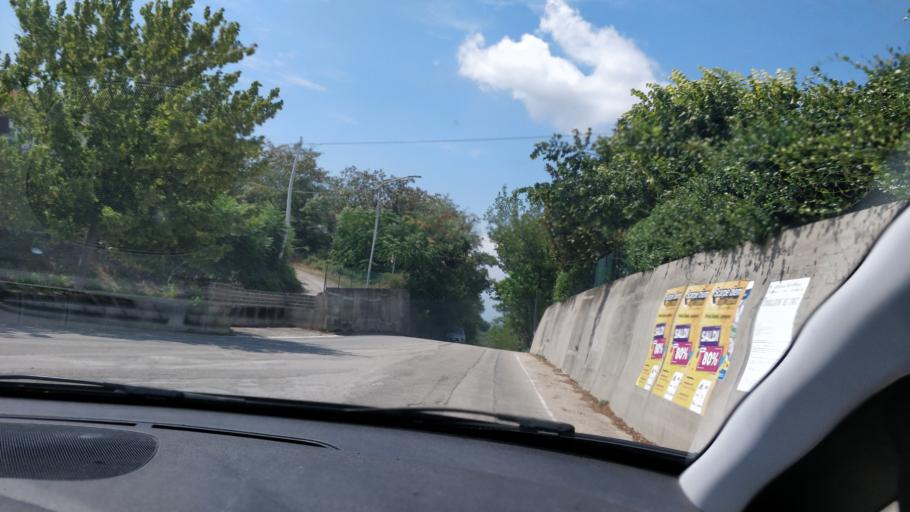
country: IT
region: Abruzzo
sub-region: Provincia di Chieti
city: Sambuceto
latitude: 42.4041
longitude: 14.1970
